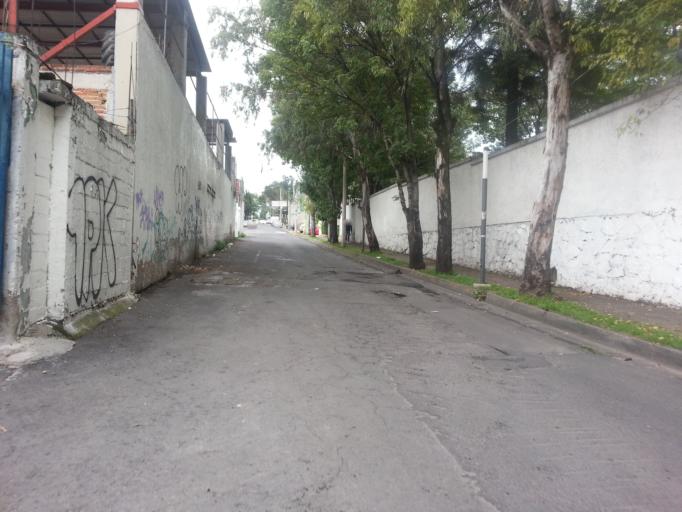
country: MX
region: Mexico City
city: Polanco
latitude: 19.3904
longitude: -99.1930
